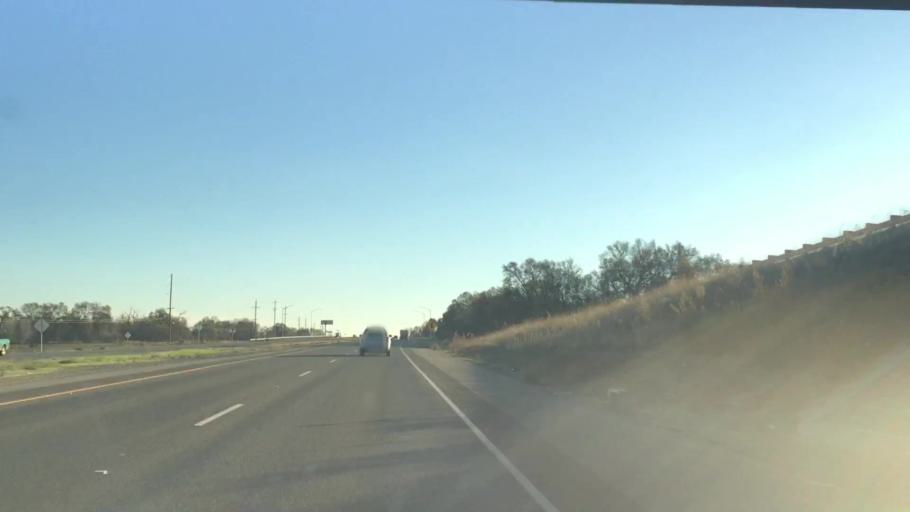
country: US
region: California
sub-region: Yuba County
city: Plumas Lake
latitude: 38.9781
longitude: -121.5432
